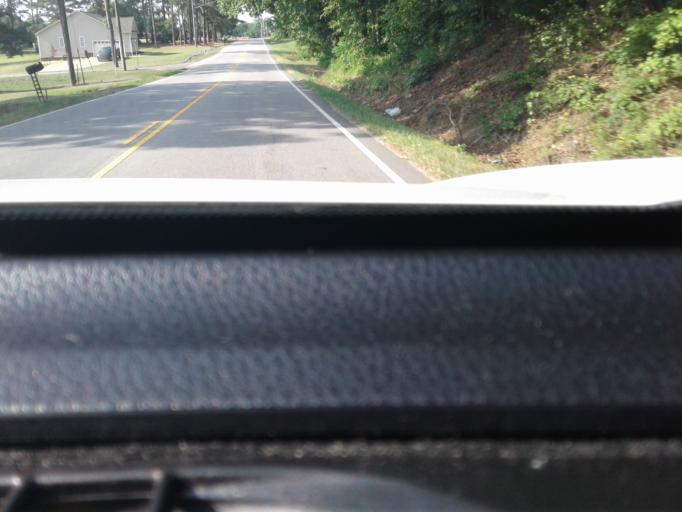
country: US
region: North Carolina
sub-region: Johnston County
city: Benson
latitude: 35.3931
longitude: -78.5432
